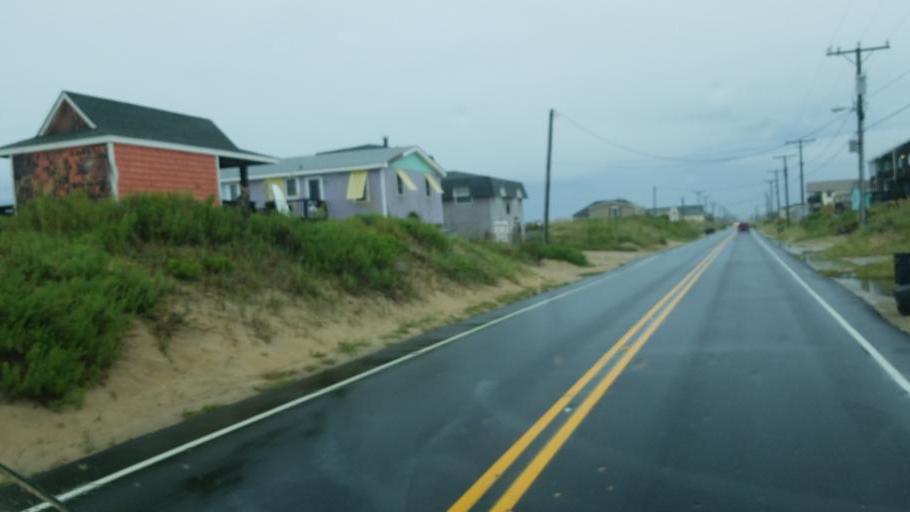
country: US
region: North Carolina
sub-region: Dare County
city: Kill Devil Hills
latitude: 36.0522
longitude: -75.6807
